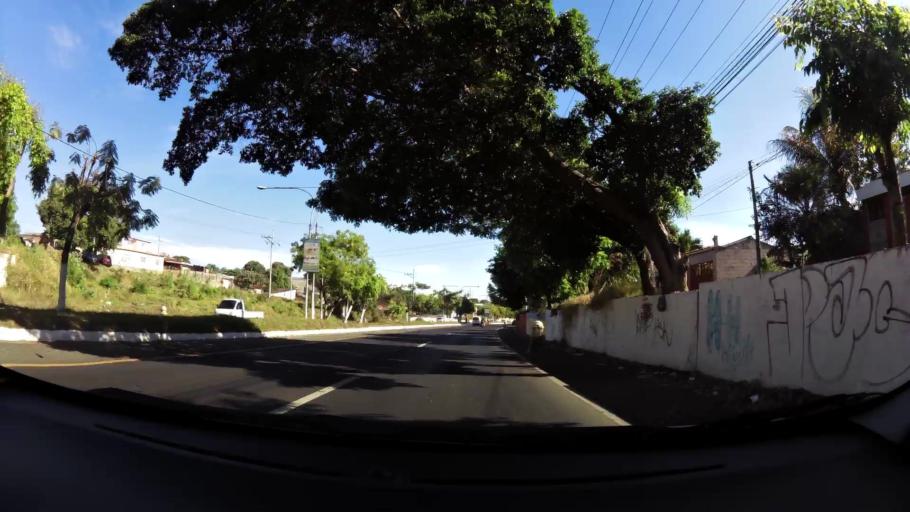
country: SV
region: Santa Ana
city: Santa Ana
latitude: 13.9826
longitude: -89.5536
